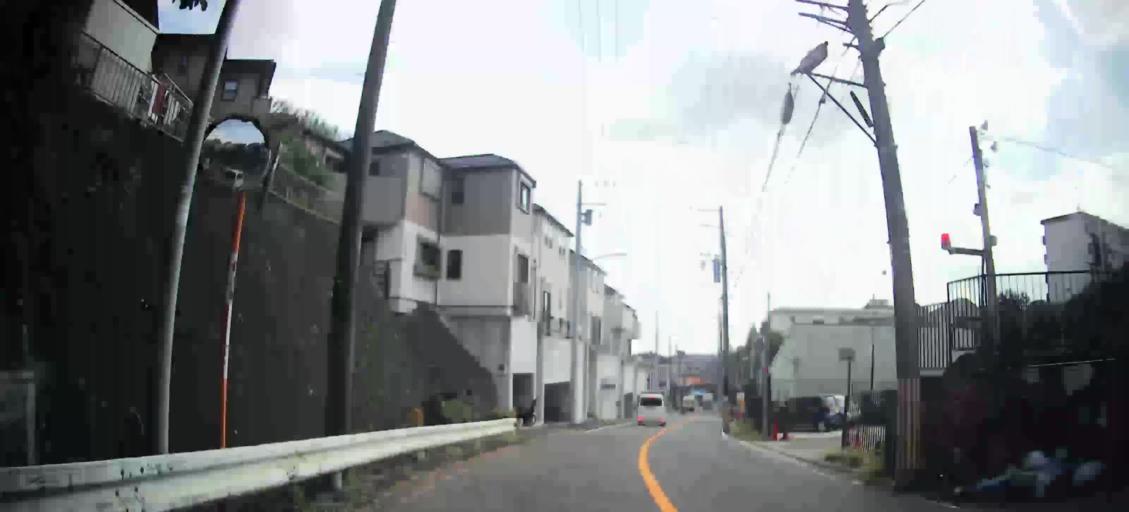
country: JP
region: Kanagawa
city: Yokohama
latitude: 35.4798
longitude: 139.5770
